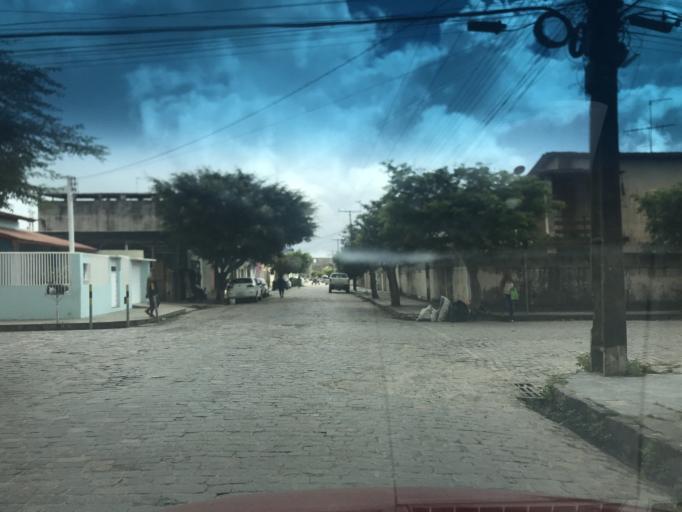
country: BR
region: Bahia
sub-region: Cruz Das Almas
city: Cruz das Almas
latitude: -12.6752
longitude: -39.0991
